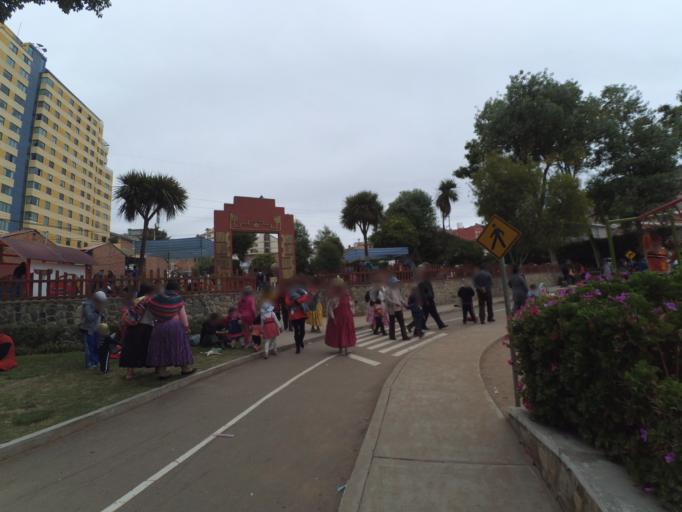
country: BO
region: La Paz
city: La Paz
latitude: -16.5417
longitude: -68.0636
